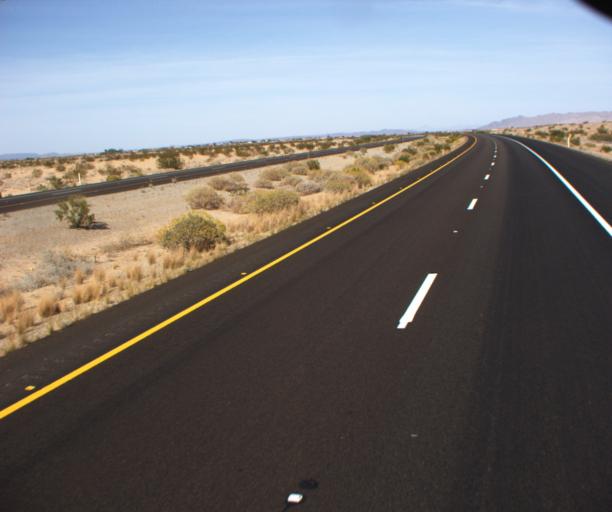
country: US
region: Arizona
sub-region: Yuma County
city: Fortuna Foothills
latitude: 32.6095
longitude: -114.5269
